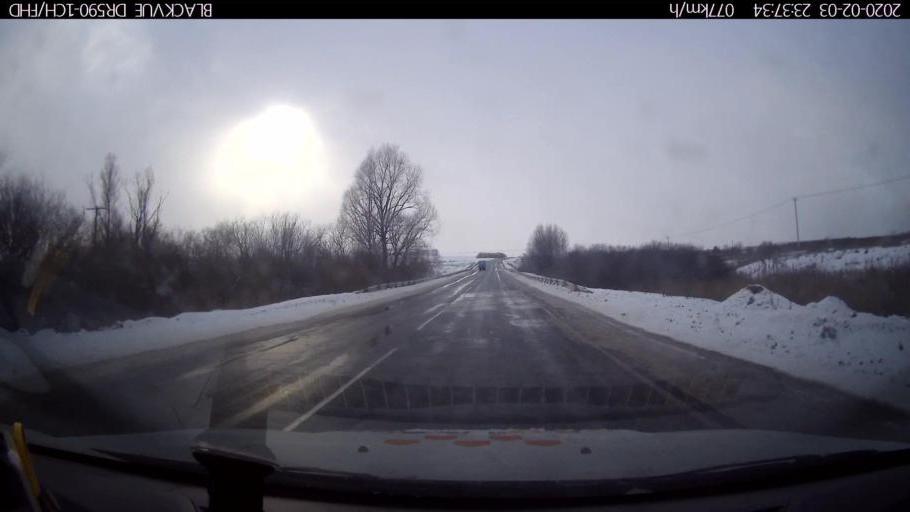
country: RU
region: Nizjnij Novgorod
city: Dal'neye Konstantinovo
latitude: 55.9008
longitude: 44.1633
